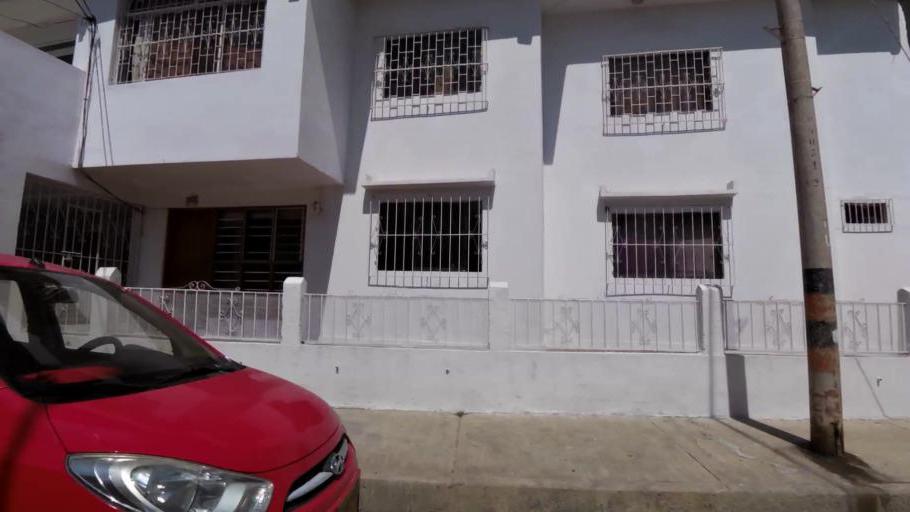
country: CO
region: Bolivar
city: Cartagena
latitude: 10.4184
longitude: -75.5311
